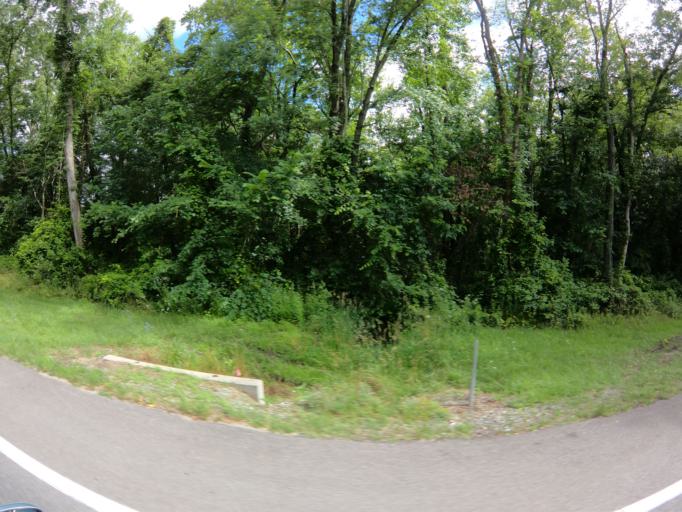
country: US
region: Maryland
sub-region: Caroline County
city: Greensboro
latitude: 39.0313
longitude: -75.7610
